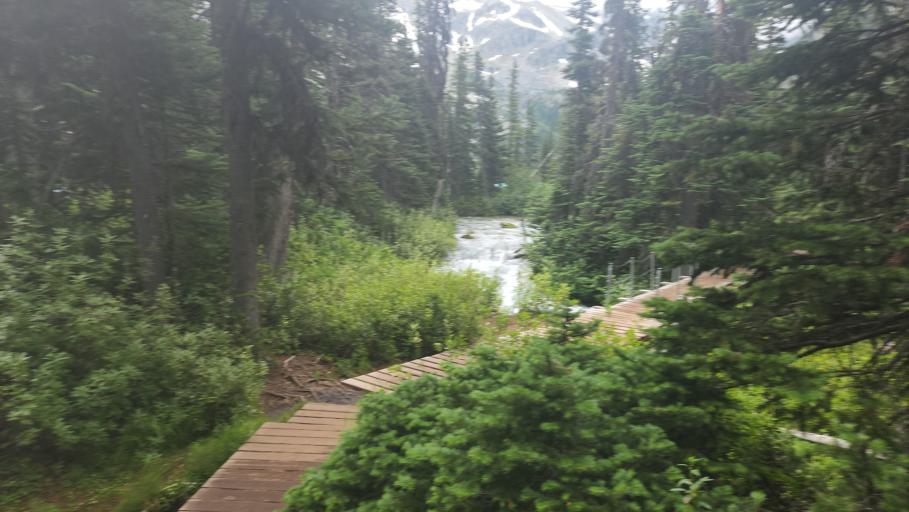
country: CA
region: British Columbia
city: Pemberton
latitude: 50.3502
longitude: -122.4782
